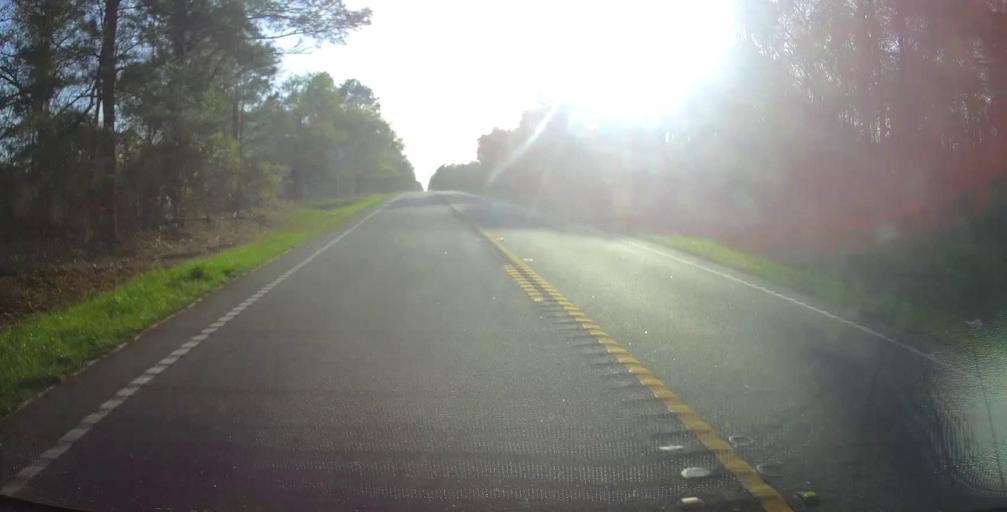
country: US
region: Georgia
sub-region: Tattnall County
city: Reidsville
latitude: 32.1441
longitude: -82.0275
